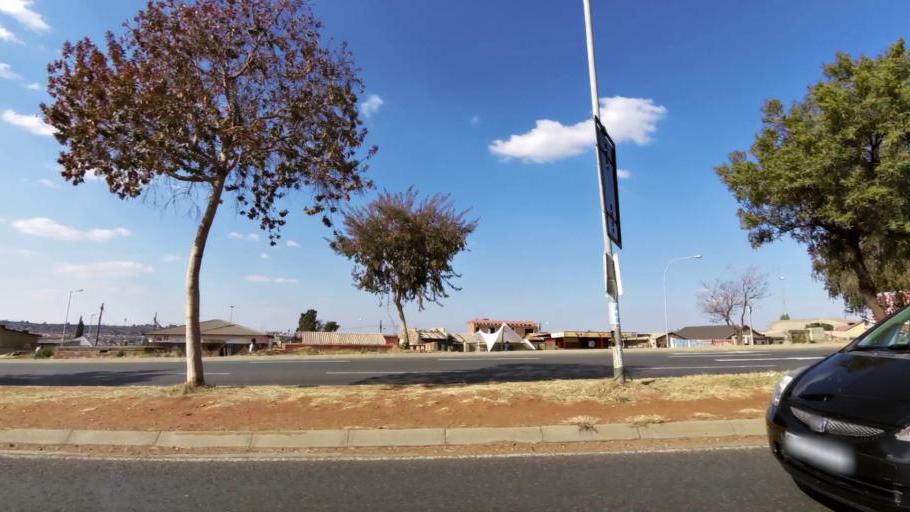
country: ZA
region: Gauteng
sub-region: City of Johannesburg Metropolitan Municipality
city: Soweto
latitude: -26.2258
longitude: 27.8730
